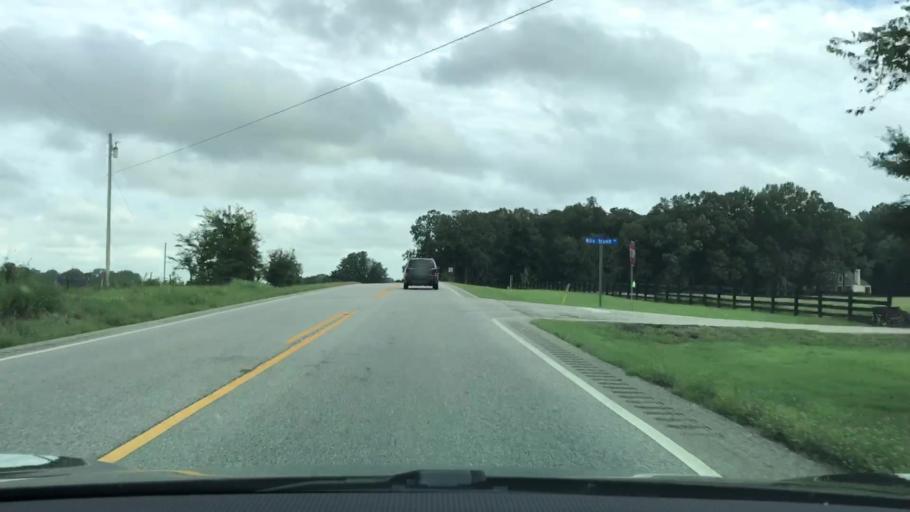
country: US
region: Alabama
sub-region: Montgomery County
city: Pike Road
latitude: 32.3251
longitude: -86.0508
